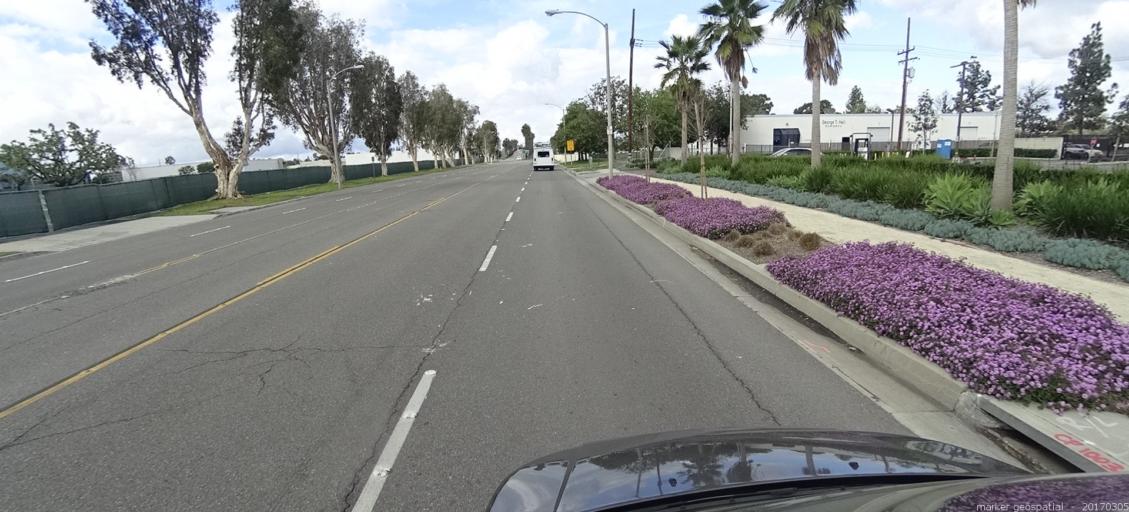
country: US
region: California
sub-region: Orange County
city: Orange
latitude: 33.7998
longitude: -117.8906
